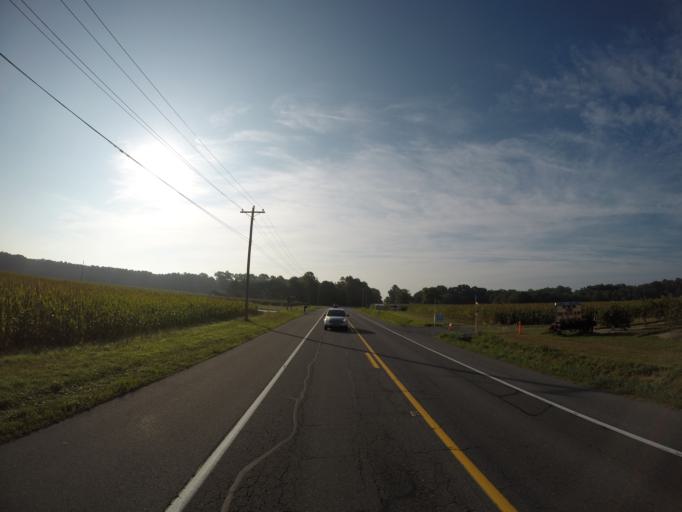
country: US
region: Delaware
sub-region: Sussex County
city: Selbyville
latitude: 38.5312
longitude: -75.2056
